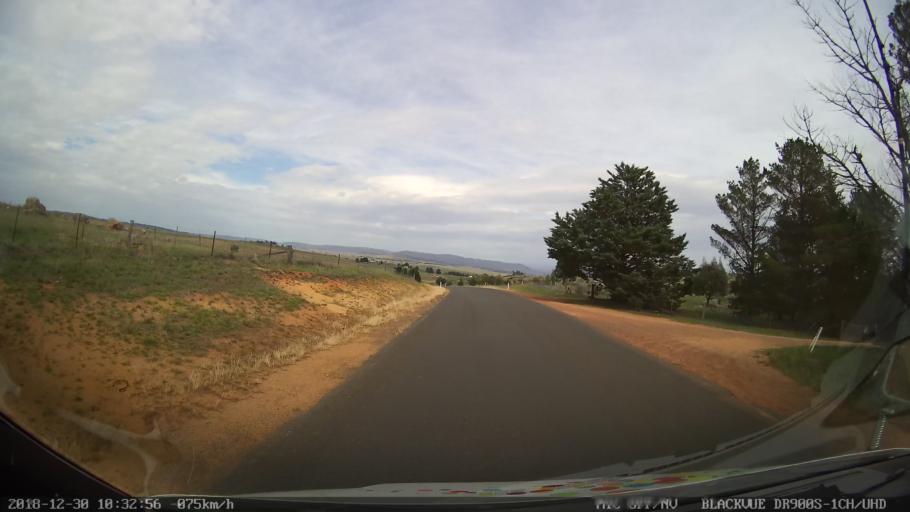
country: AU
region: New South Wales
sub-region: Snowy River
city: Berridale
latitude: -36.4985
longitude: 148.8600
